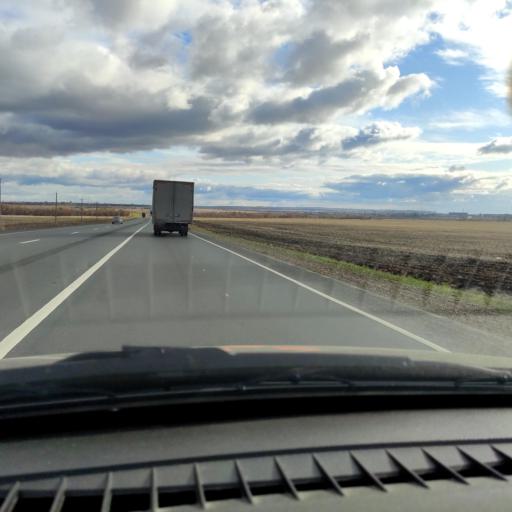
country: RU
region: Samara
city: Varlamovo
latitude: 53.2113
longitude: 48.4557
